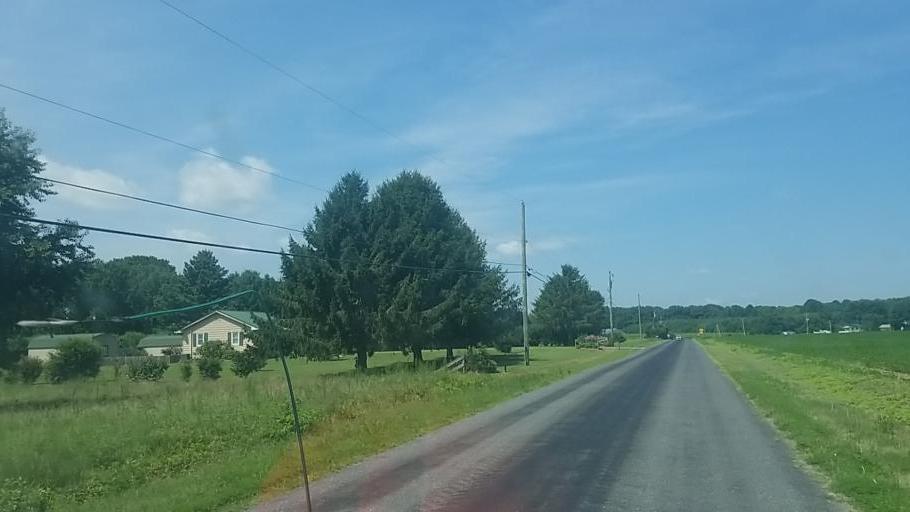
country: US
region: Maryland
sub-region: Caroline County
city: Denton
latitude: 38.8784
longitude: -75.7917
